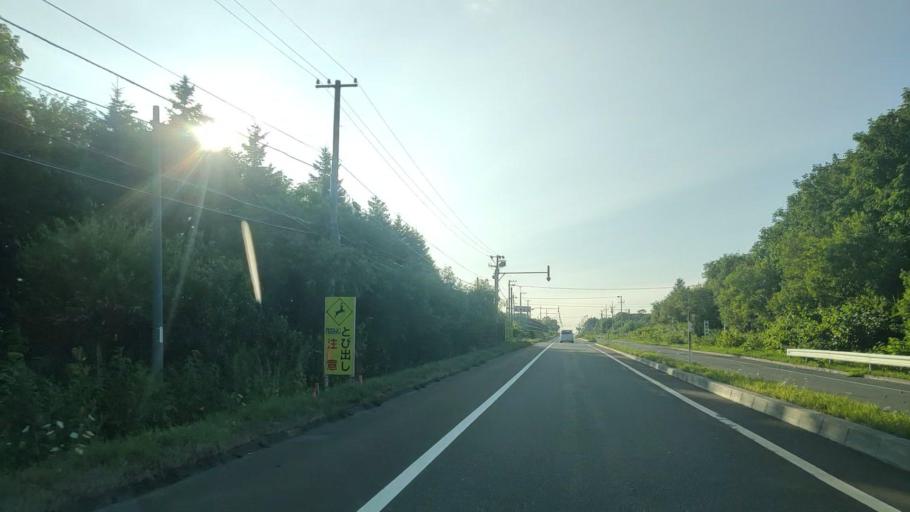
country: JP
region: Hokkaido
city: Wakkanai
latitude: 45.3699
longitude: 141.7244
